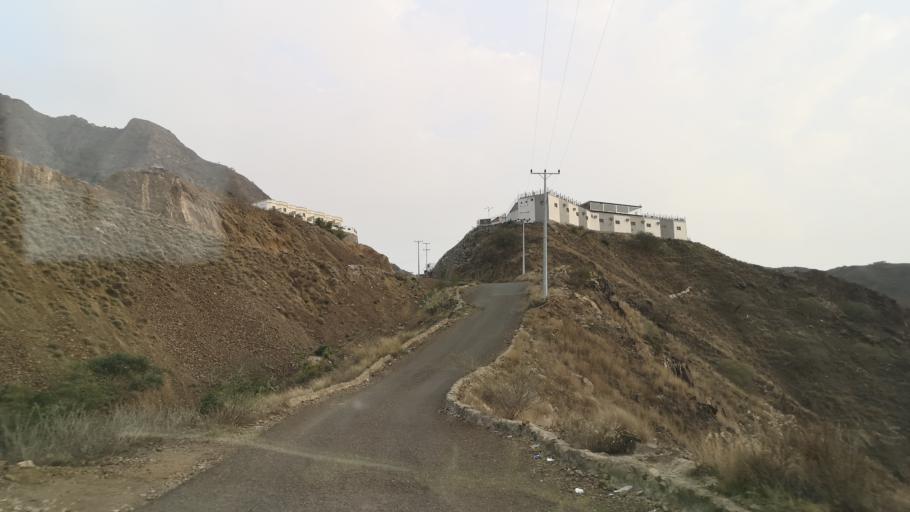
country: YE
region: Sa'dah
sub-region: Monabbih
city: Suq al Khamis
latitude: 17.3253
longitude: 43.1468
